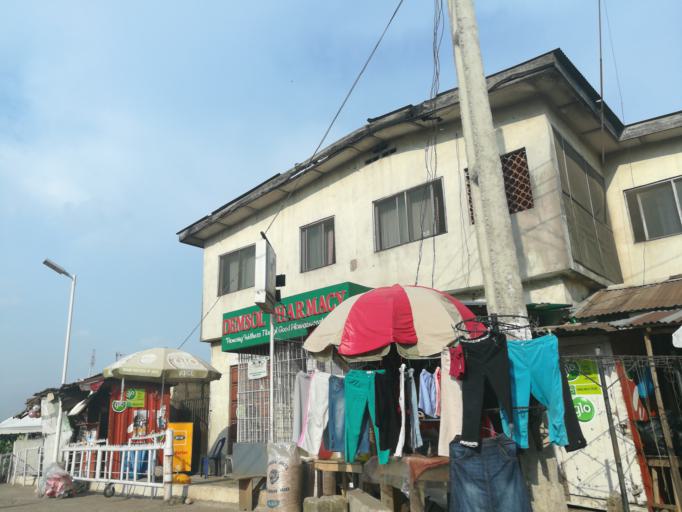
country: NG
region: Lagos
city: Ojota
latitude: 6.5949
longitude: 3.4006
